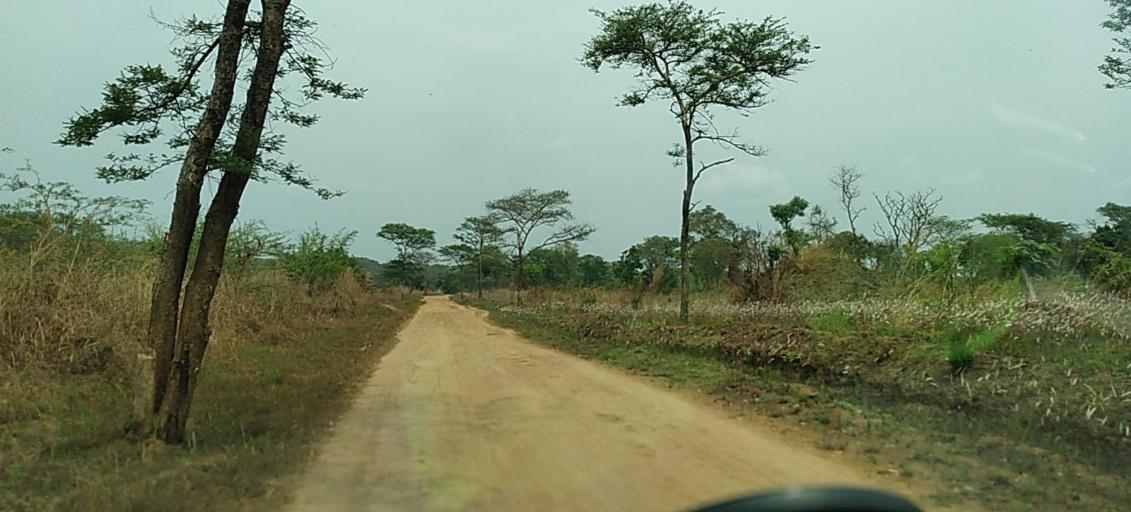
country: ZM
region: North-Western
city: Solwezi
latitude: -12.7925
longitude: 26.5309
